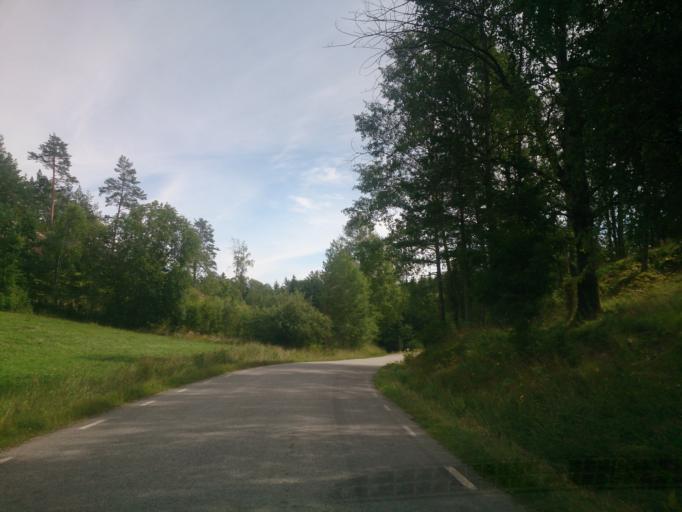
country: SE
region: OEstergoetland
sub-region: Valdemarsviks Kommun
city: Gusum
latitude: 58.3123
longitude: 16.3427
